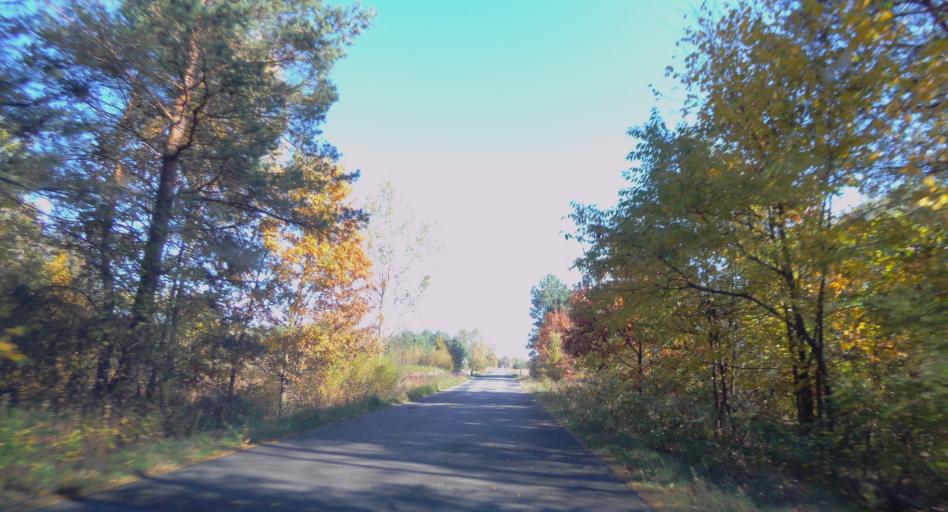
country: PL
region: Subcarpathian Voivodeship
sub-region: Powiat lezajski
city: Wola Zarczycka
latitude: 50.2670
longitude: 22.2498
